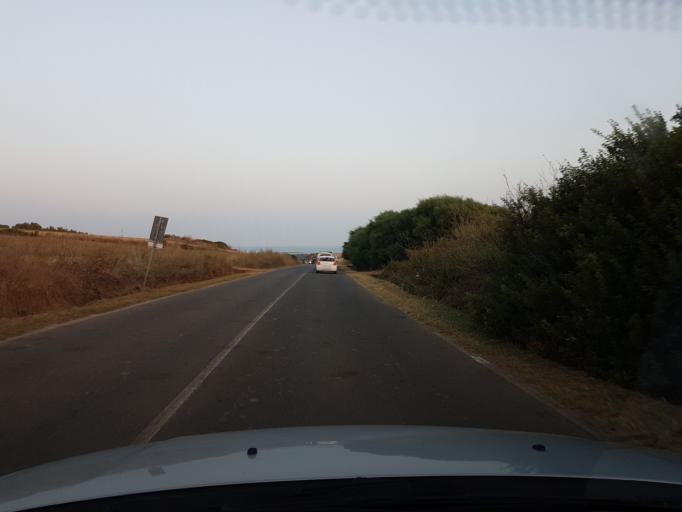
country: IT
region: Sardinia
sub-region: Provincia di Oristano
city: Cabras
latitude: 39.9338
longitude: 8.4477
